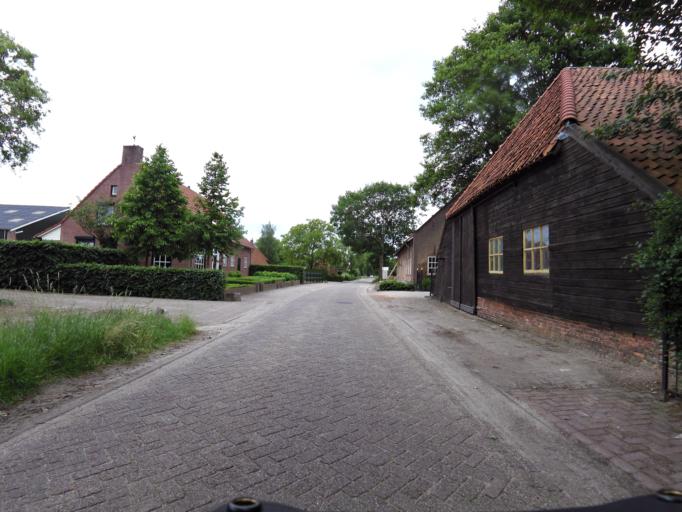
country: NL
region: North Brabant
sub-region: Gemeente Baarle-Nassau
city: Baarle-Nassau
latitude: 51.4737
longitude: 4.9498
